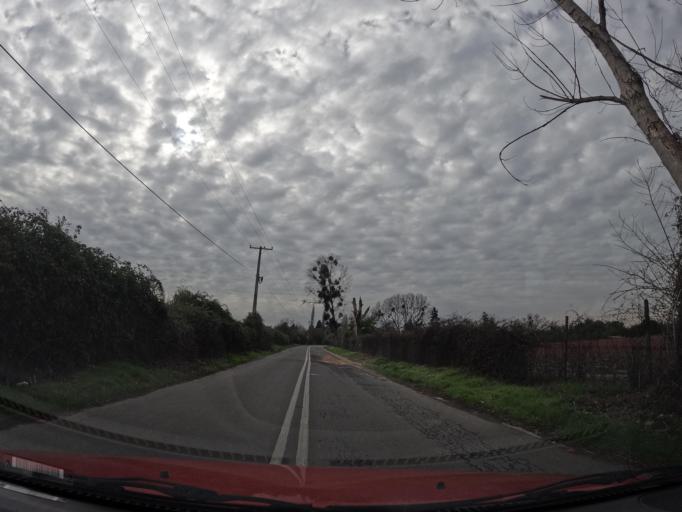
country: CL
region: Maule
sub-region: Provincia de Linares
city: Linares
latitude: -35.8569
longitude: -71.6154
